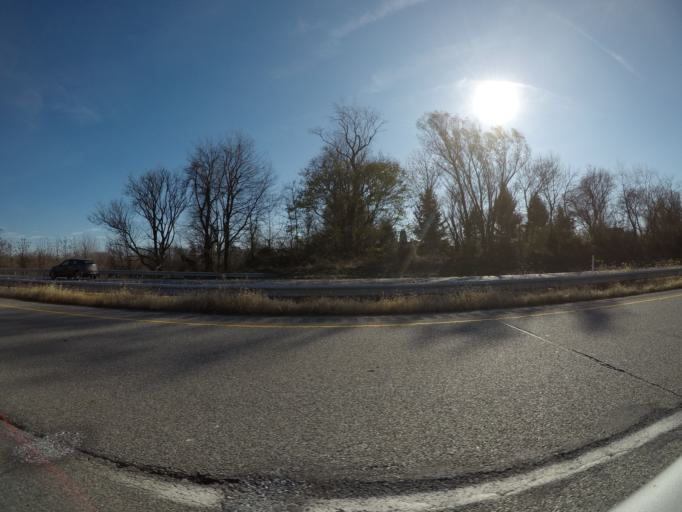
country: US
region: Pennsylvania
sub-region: Chester County
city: Parkesburg
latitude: 39.9853
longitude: -75.8992
